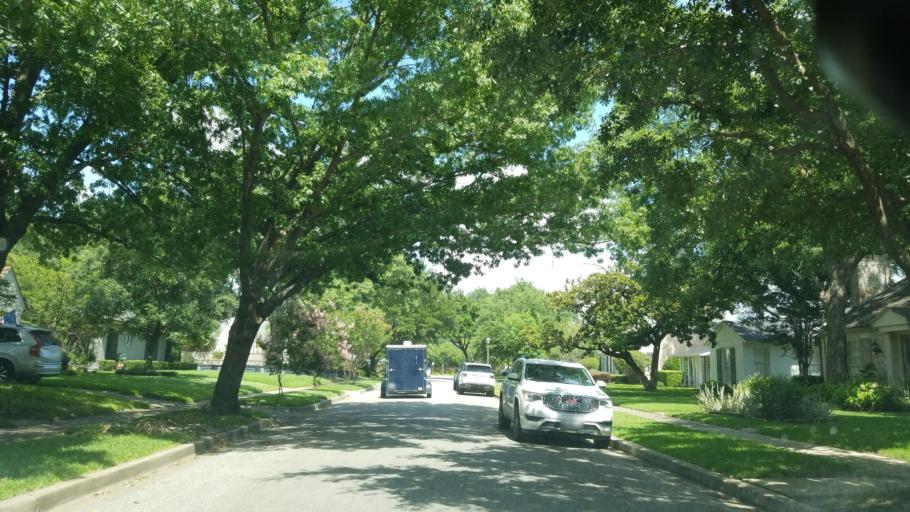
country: US
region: Texas
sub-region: Dallas County
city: Highland Park
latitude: 32.8305
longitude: -96.8176
